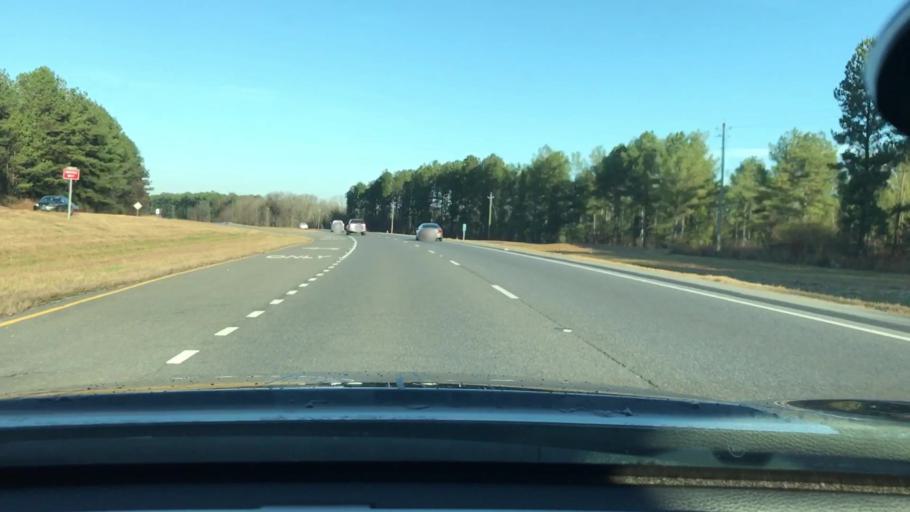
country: US
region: Alabama
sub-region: Talladega County
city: Childersburg
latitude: 33.3010
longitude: -86.3698
